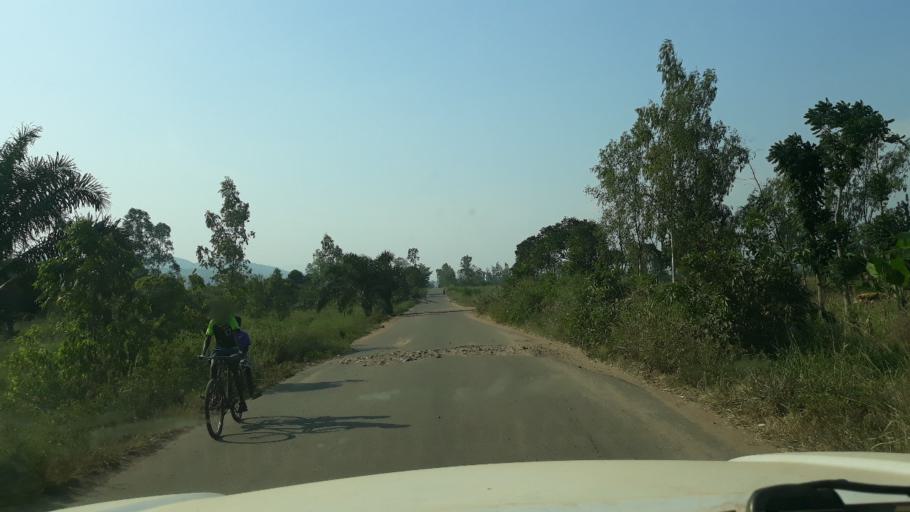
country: BI
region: Cibitoke
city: Cibitoke
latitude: -2.7637
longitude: 28.9998
